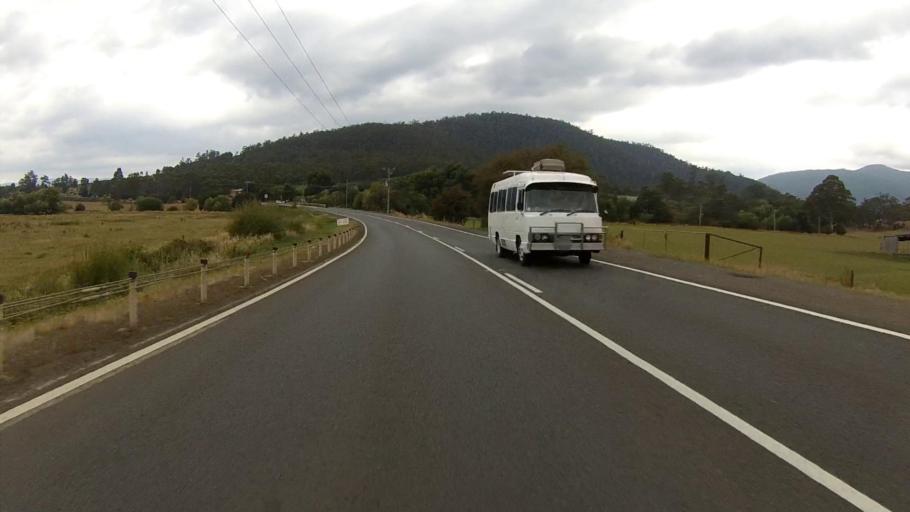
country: AU
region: Tasmania
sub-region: Huon Valley
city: Franklin
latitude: -43.0714
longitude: 147.0393
